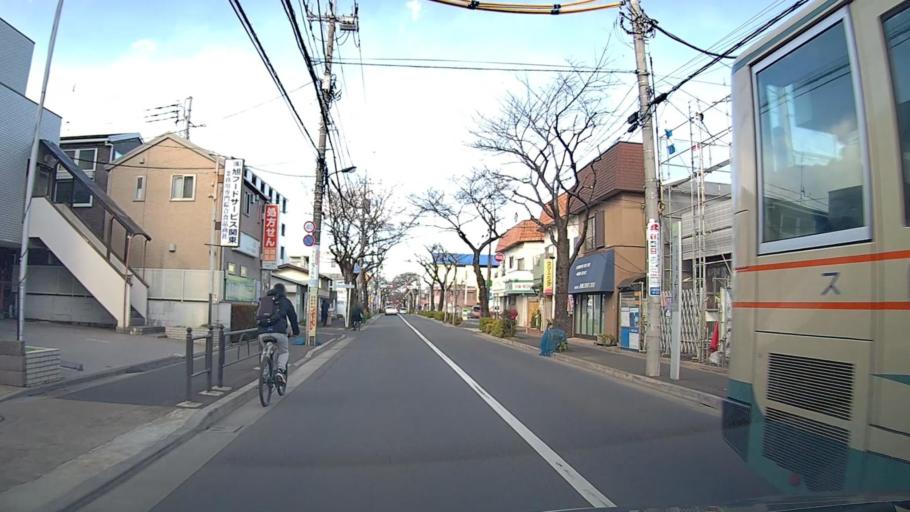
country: JP
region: Saitama
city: Asaka
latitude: 35.7665
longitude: 139.5875
